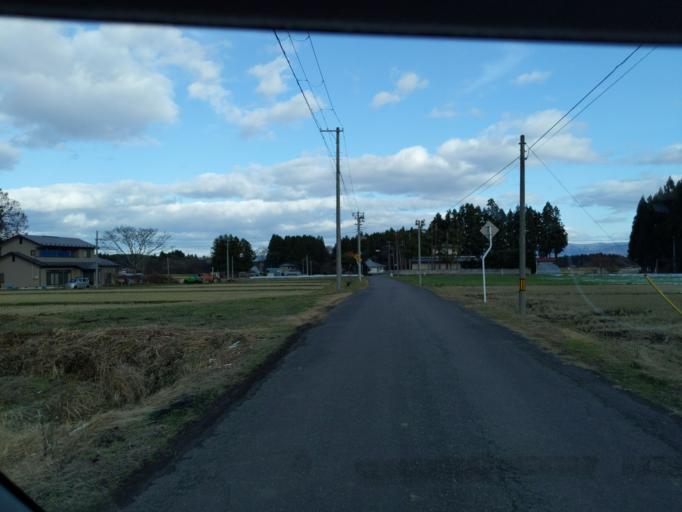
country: JP
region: Iwate
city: Mizusawa
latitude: 39.1113
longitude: 141.0909
